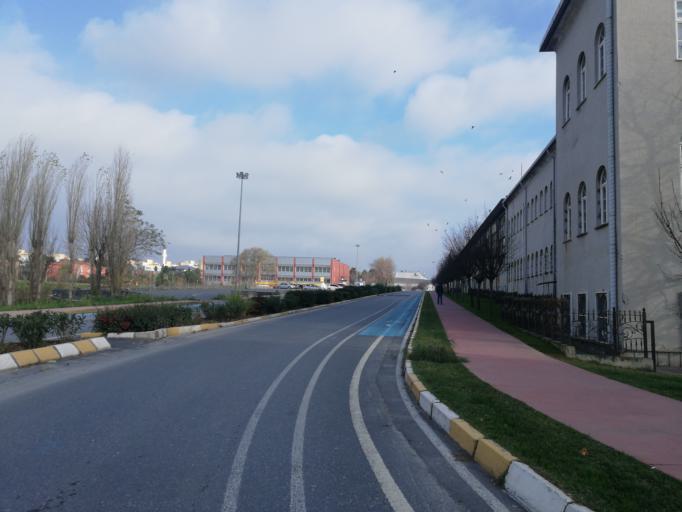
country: TR
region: Istanbul
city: merter keresteciler
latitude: 41.0251
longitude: 28.8870
